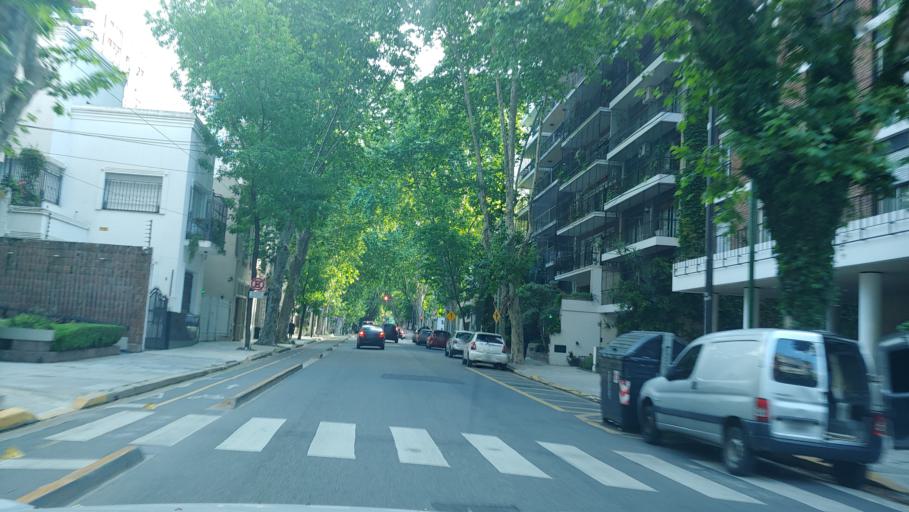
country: AR
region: Buenos Aires F.D.
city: Colegiales
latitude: -34.5667
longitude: -58.4430
